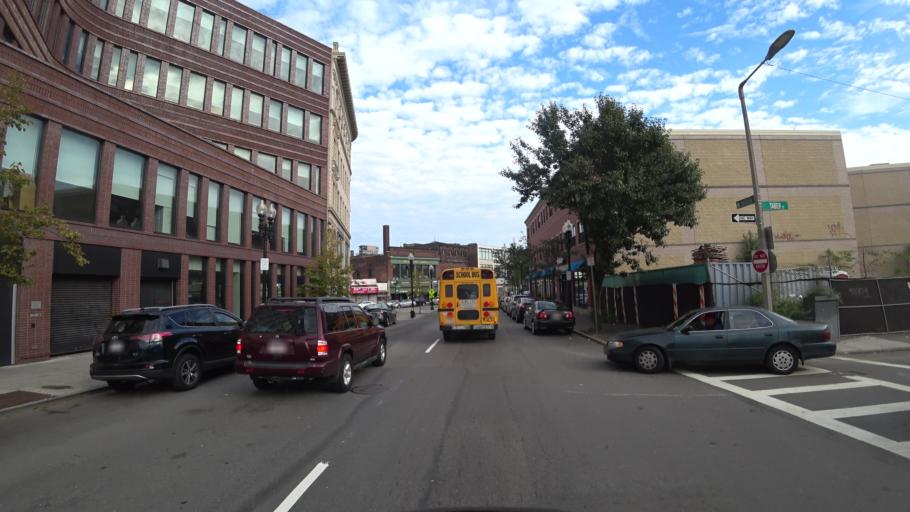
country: US
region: Massachusetts
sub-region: Suffolk County
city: South Boston
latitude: 42.3300
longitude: -71.0832
